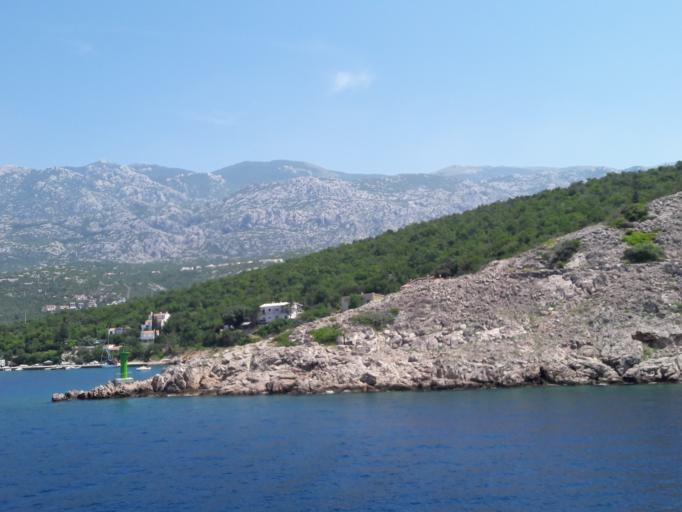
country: HR
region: Primorsko-Goranska
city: Banjol
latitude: 44.7177
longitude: 14.8879
